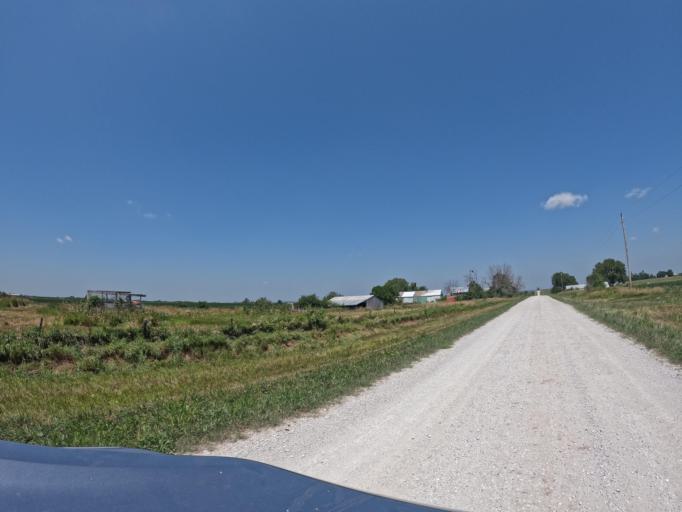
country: US
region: Iowa
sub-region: Keokuk County
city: Sigourney
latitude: 41.2680
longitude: -92.1700
